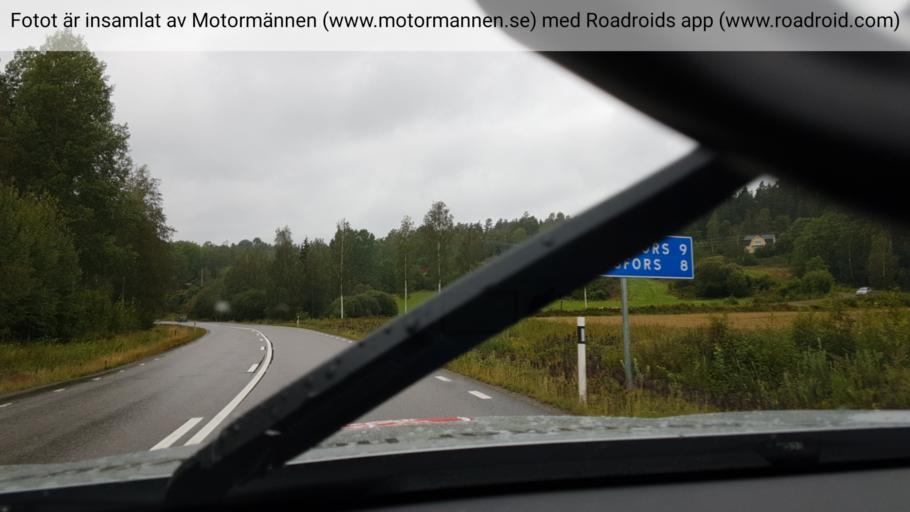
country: SE
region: Vaestra Goetaland
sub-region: Bengtsfors Kommun
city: Billingsfors
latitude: 59.0375
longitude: 12.3255
